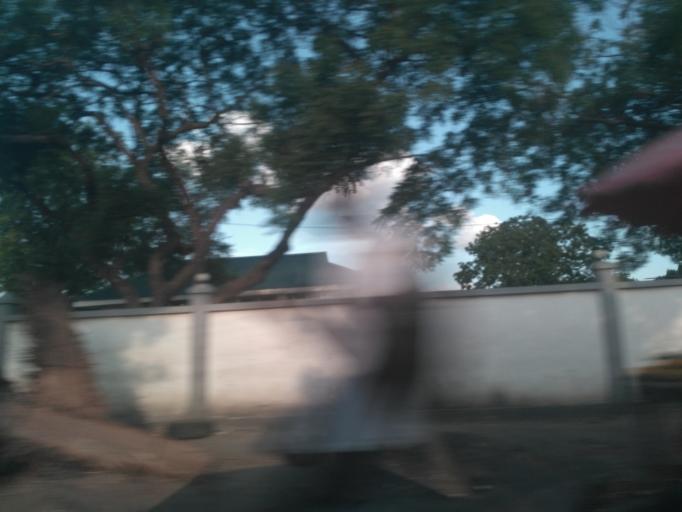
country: TZ
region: Dar es Salaam
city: Dar es Salaam
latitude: -6.8583
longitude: 39.2610
